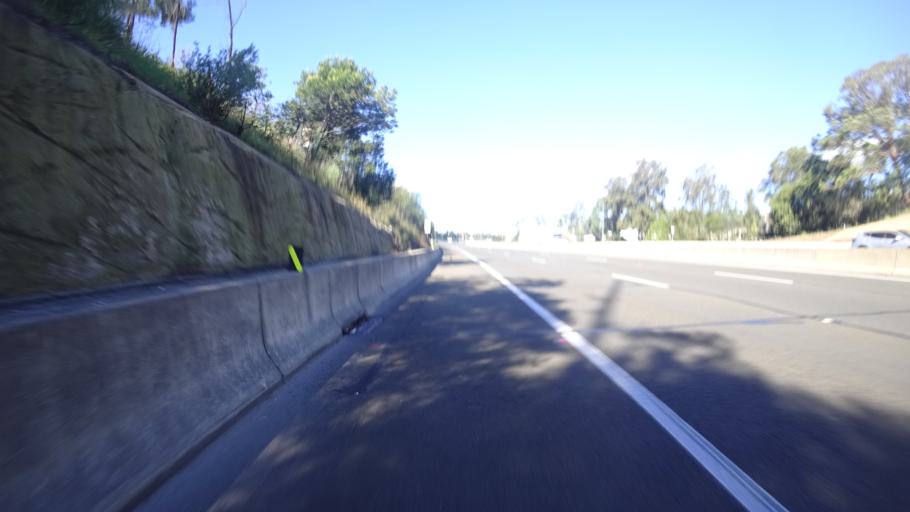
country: AU
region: New South Wales
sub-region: Ryde
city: Macquarie Park
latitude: -33.7725
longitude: 151.1194
